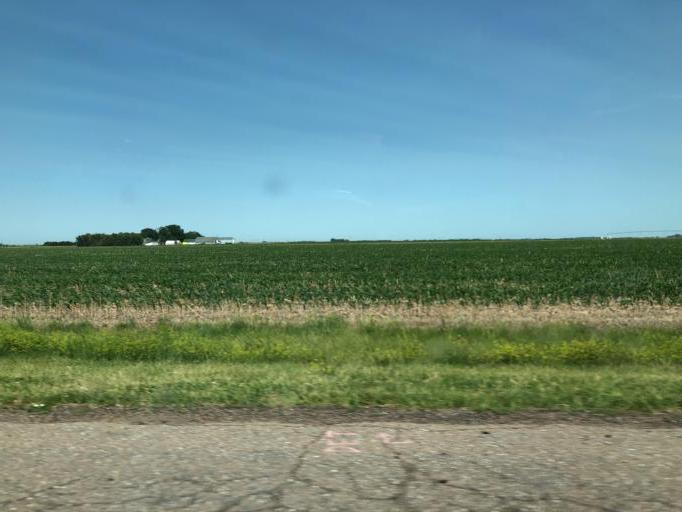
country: US
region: Nebraska
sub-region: Thayer County
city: Hebron
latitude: 40.3188
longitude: -97.5765
